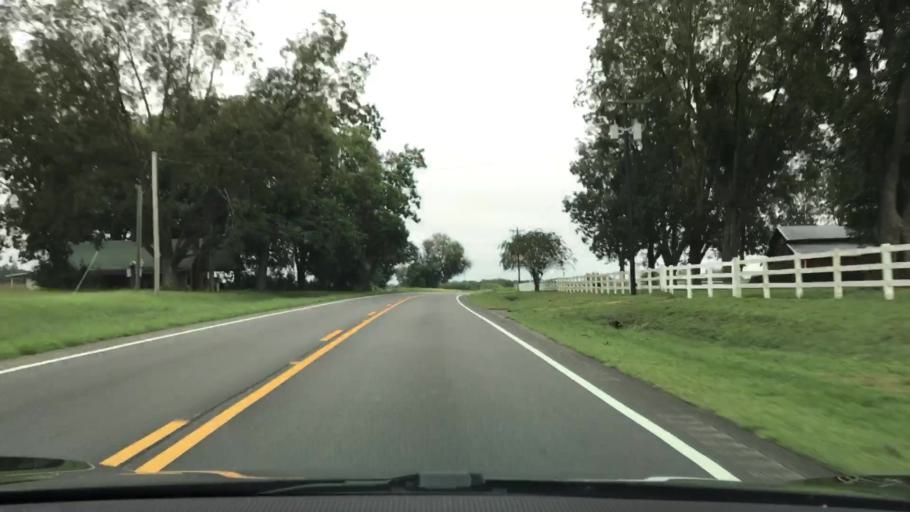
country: US
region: Alabama
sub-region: Covington County
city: Opp
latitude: 31.2351
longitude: -86.1621
